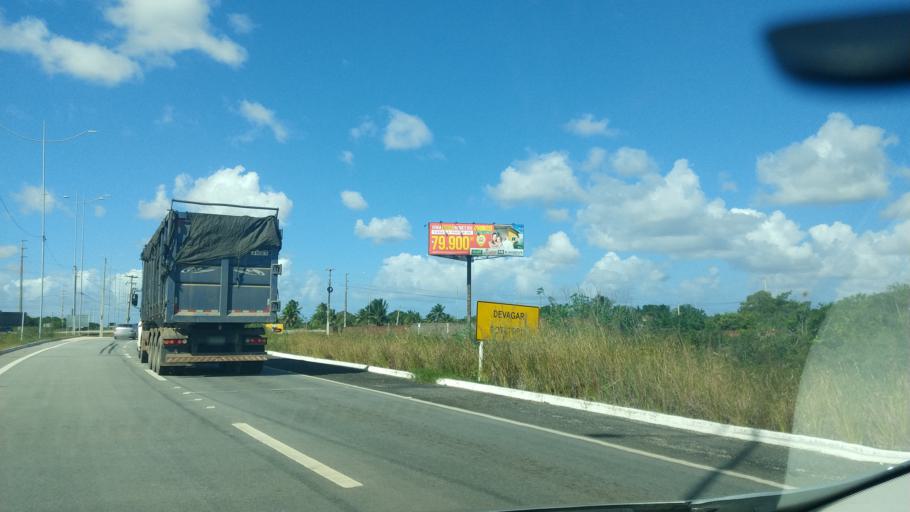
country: BR
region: Rio Grande do Norte
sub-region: Sao Goncalo Do Amarante
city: Sao Goncalo do Amarante
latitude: -5.7715
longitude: -35.3380
